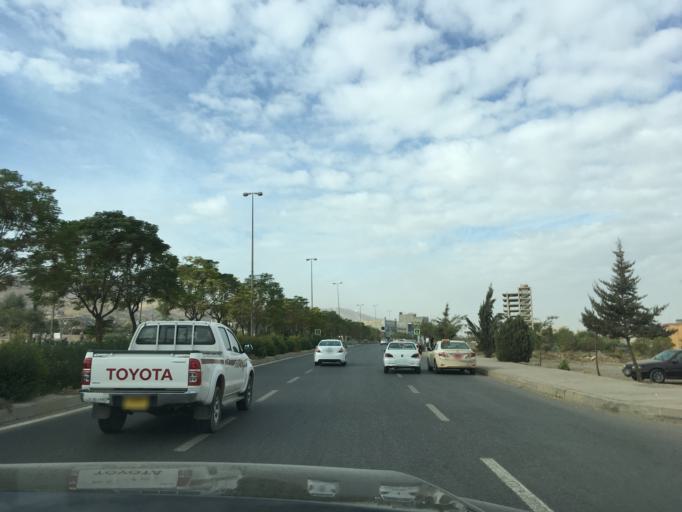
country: IQ
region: Dahuk
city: Sinah
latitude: 36.8470
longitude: 43.0359
